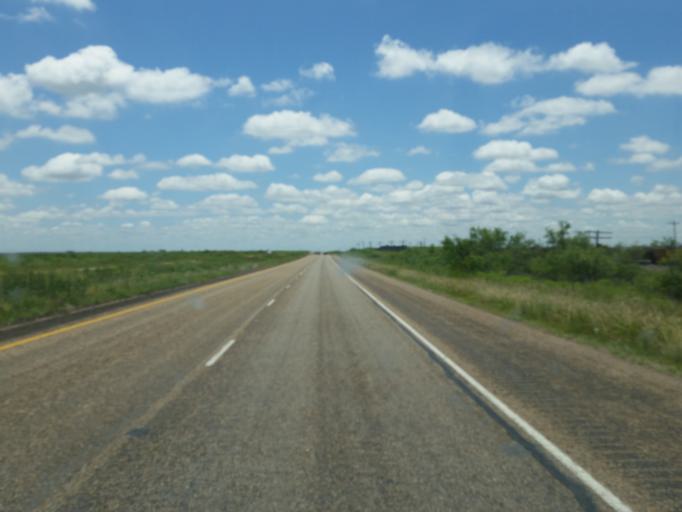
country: US
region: Texas
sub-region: Garza County
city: Post
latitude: 33.1286
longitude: -101.2964
